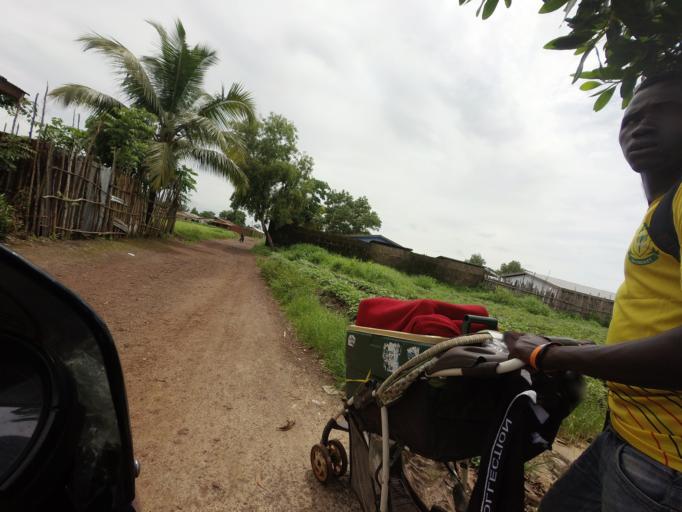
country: SL
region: Northern Province
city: Kambia
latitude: 9.1048
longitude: -12.9253
